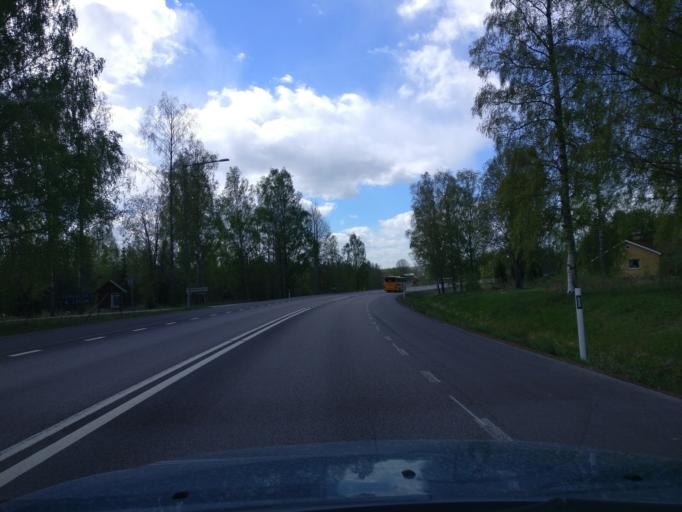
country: SE
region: Vaermland
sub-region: Karlstads Kommun
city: Molkom
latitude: 59.5991
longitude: 13.7362
